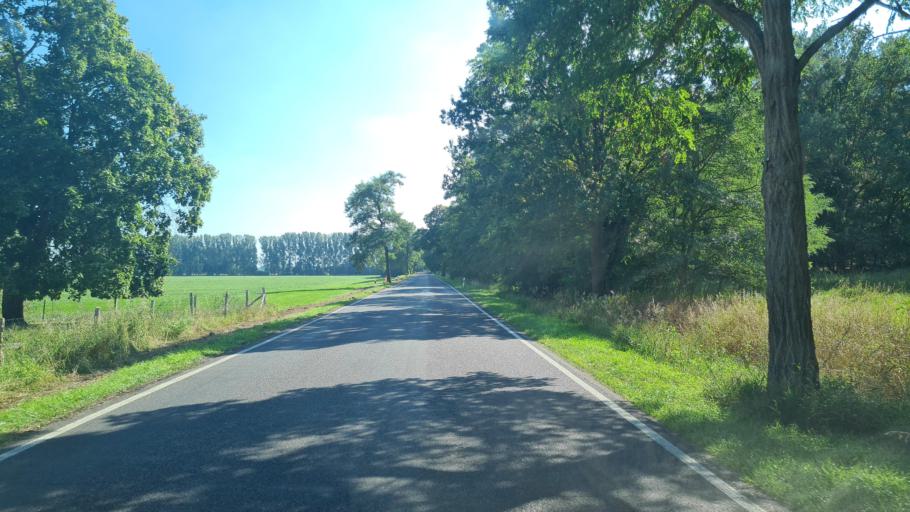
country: DE
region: Brandenburg
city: Friesack
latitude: 52.7225
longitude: 12.6332
